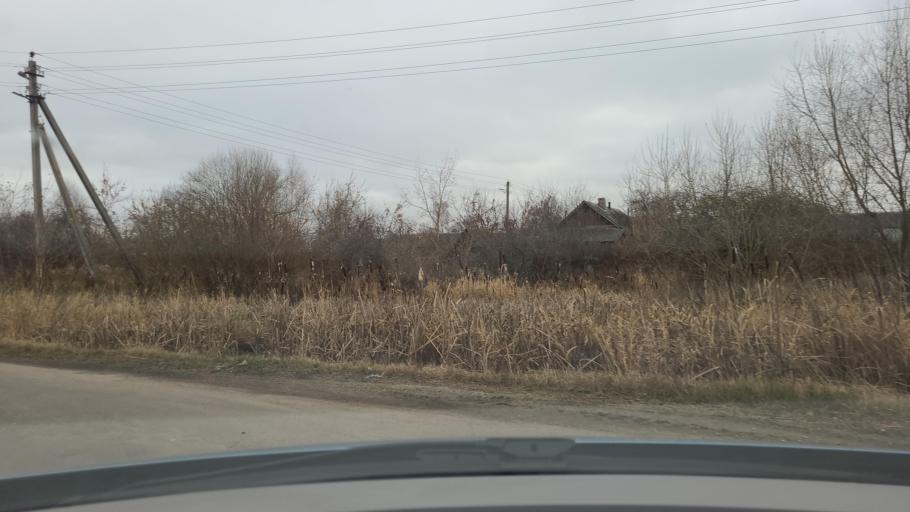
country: BY
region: Minsk
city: Khalopyenichy
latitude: 54.5134
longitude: 28.9549
